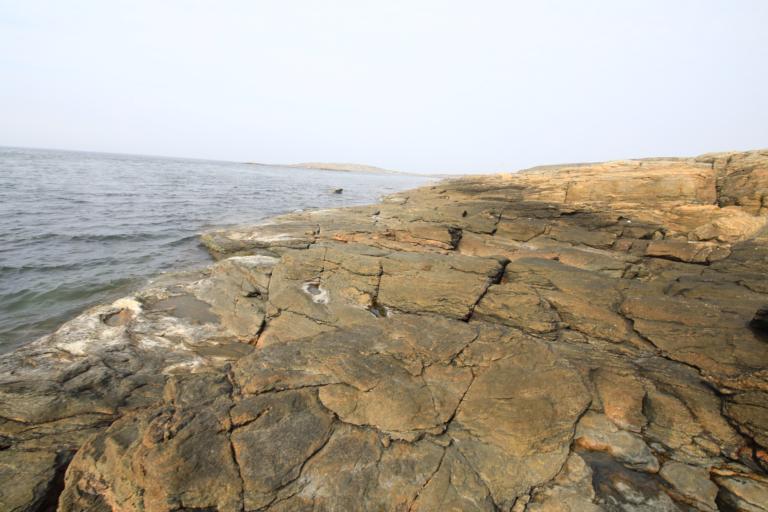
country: SE
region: Halland
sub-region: Kungsbacka Kommun
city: Frillesas
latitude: 57.2491
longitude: 12.0910
